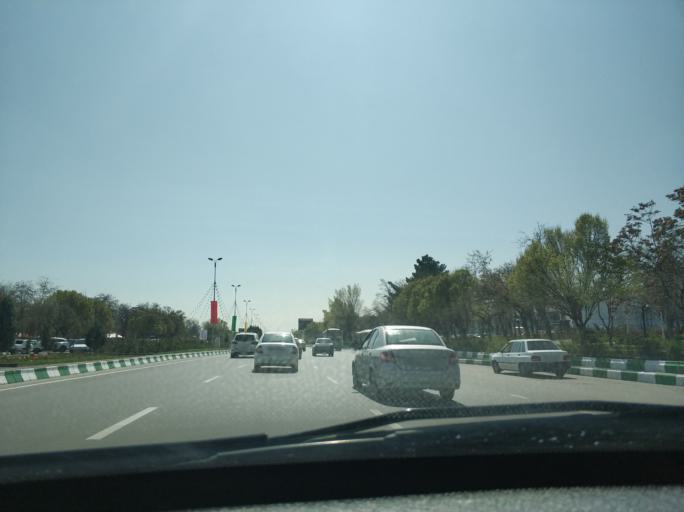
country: IR
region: Razavi Khorasan
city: Mashhad
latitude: 36.2573
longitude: 59.6093
